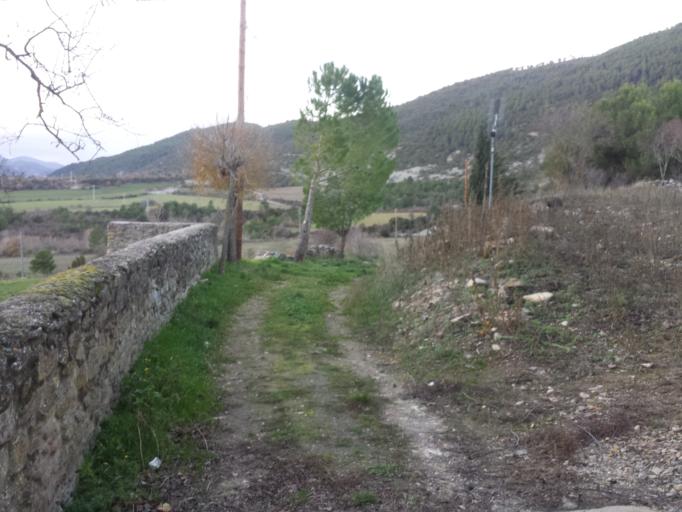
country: ES
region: Aragon
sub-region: Provincia de Zaragoza
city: Santa Eulalia de Gallego
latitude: 42.3870
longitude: -0.7191
